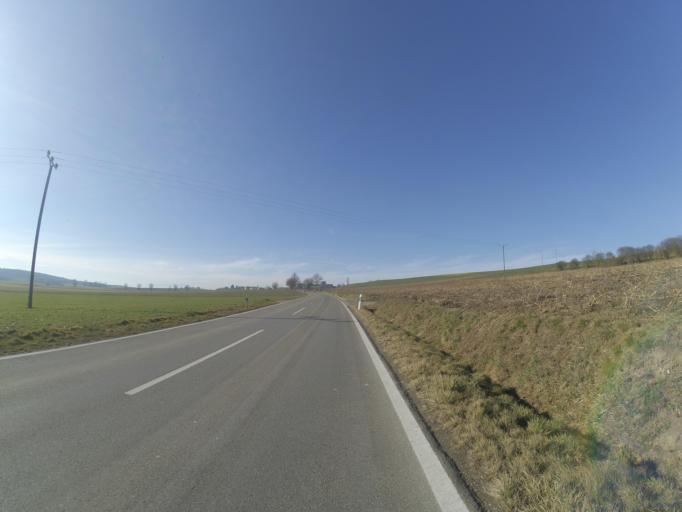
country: DE
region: Baden-Wuerttemberg
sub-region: Tuebingen Region
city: Aulendorf
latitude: 47.9248
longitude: 9.6333
